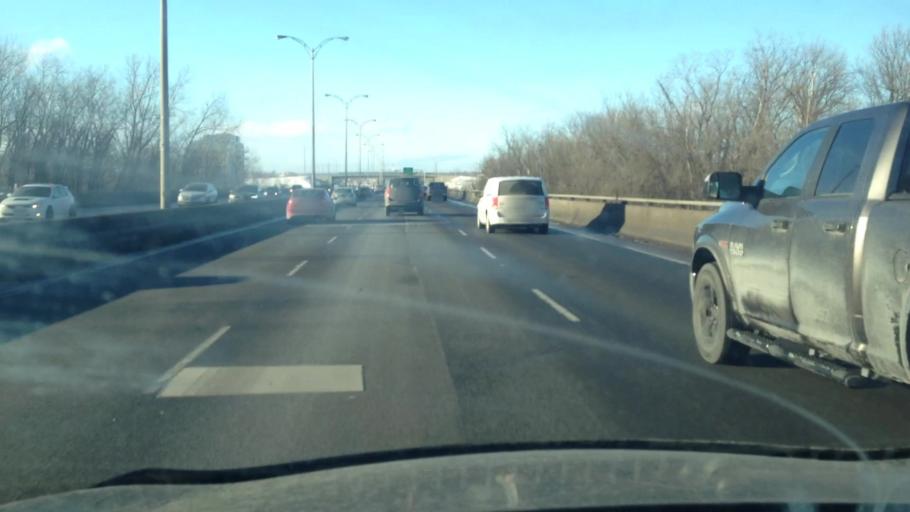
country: CA
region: Quebec
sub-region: Laurentides
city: Boisbriand
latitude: 45.6122
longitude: -73.8156
